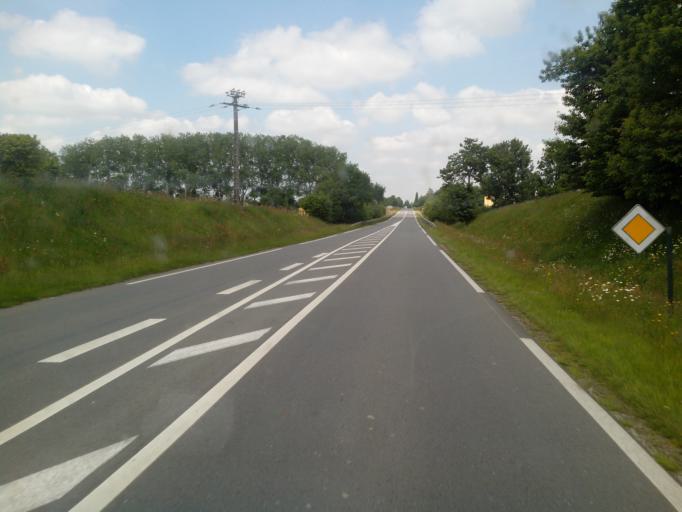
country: FR
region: Brittany
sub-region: Departement d'Ille-et-Vilaine
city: Saint-Germain-en-Cogles
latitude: 48.3868
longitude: -1.2753
